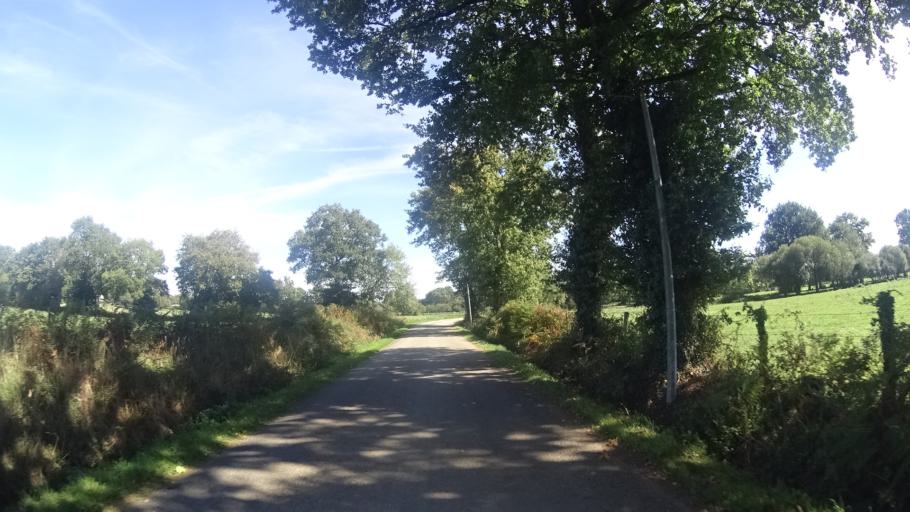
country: FR
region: Brittany
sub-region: Departement du Morbihan
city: Peillac
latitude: 47.7322
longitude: -2.1874
